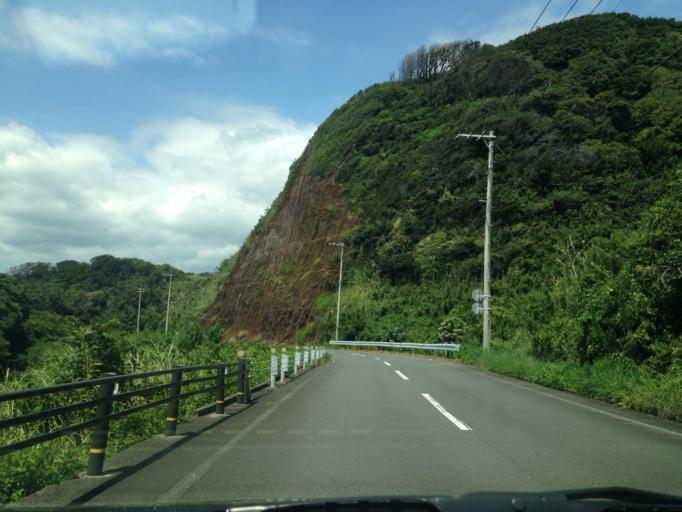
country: JP
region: Shizuoka
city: Shimoda
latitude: 34.6129
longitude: 138.8272
